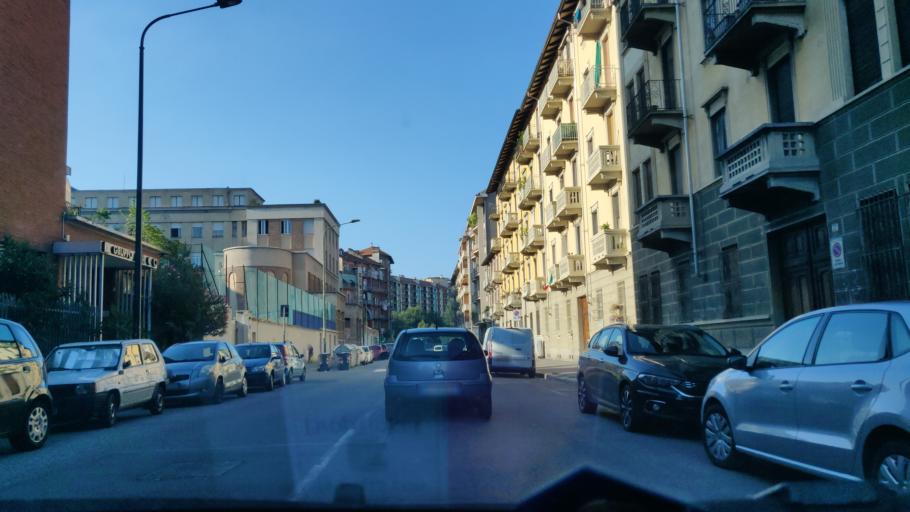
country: IT
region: Piedmont
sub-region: Provincia di Torino
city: Lesna
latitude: 45.0716
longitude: 7.6423
